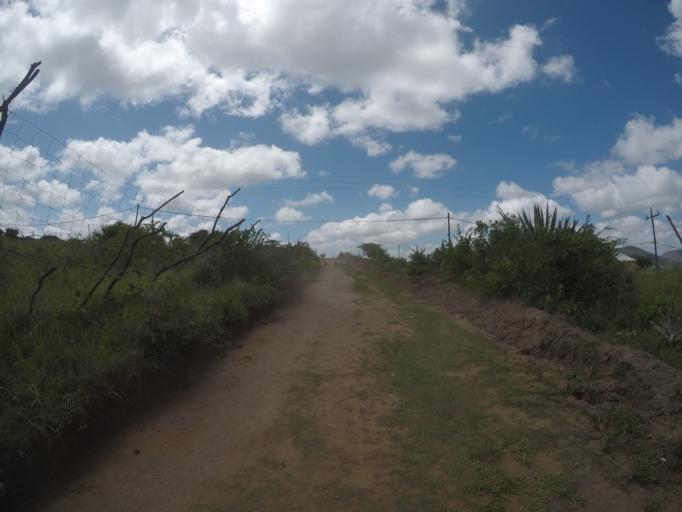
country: ZA
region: KwaZulu-Natal
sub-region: uThungulu District Municipality
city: Empangeni
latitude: -28.5832
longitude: 31.8432
